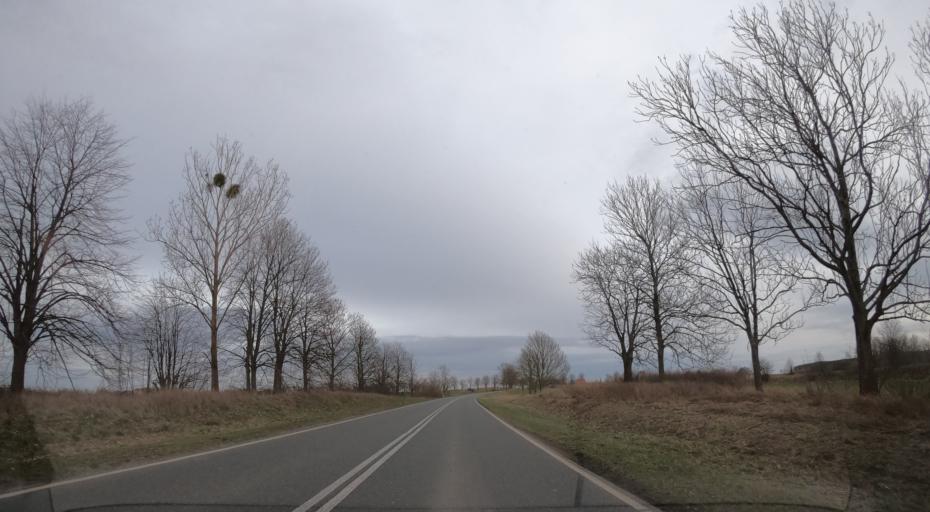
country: PL
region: West Pomeranian Voivodeship
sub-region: Powiat mysliborski
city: Nowogrodek Pomorski
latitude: 52.9008
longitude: 14.9898
